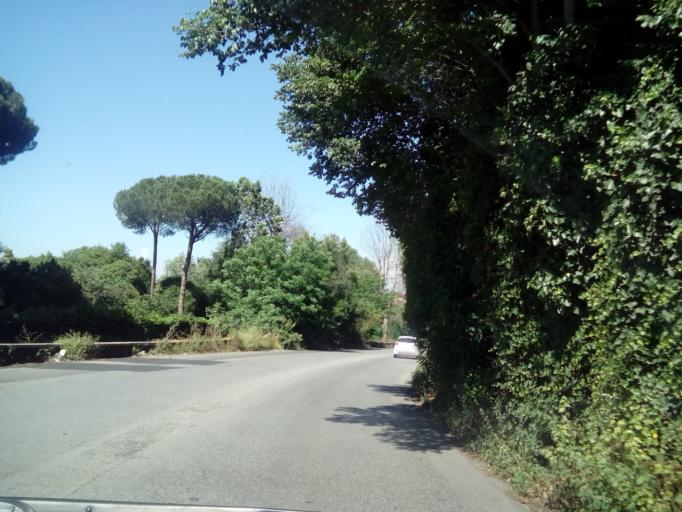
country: VA
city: Vatican City
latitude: 41.8445
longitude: 12.4696
